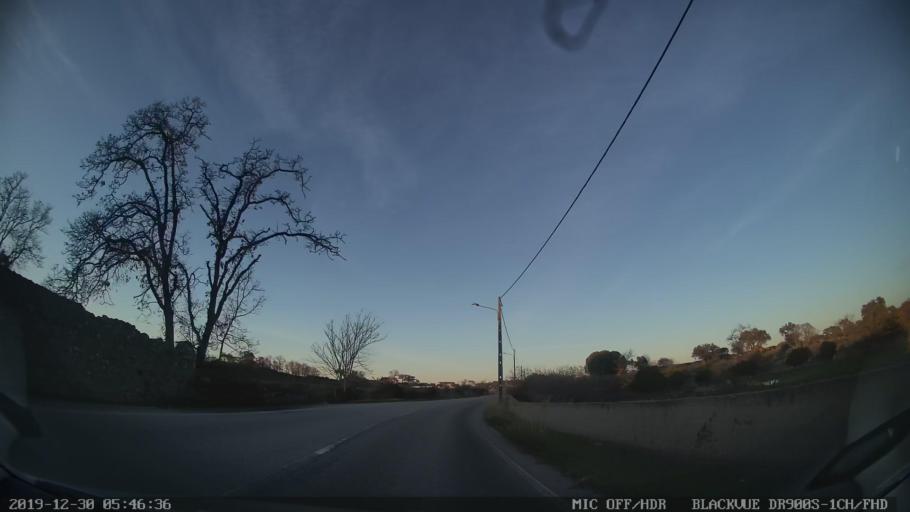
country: PT
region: Castelo Branco
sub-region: Idanha-A-Nova
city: Idanha-a-Nova
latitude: 39.9438
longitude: -7.2365
